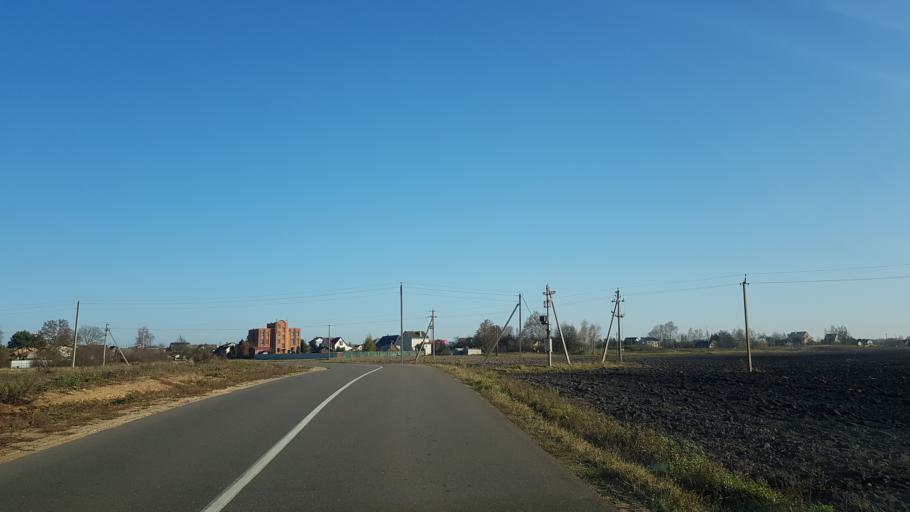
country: BY
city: Fanipol
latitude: 53.7198
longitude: 27.3092
